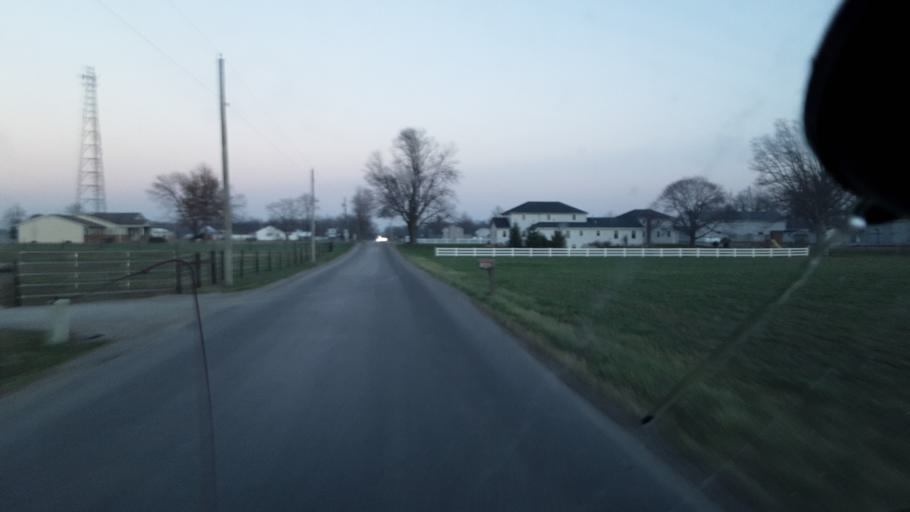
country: US
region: Indiana
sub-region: Allen County
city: Harlan
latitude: 41.2394
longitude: -84.9296
